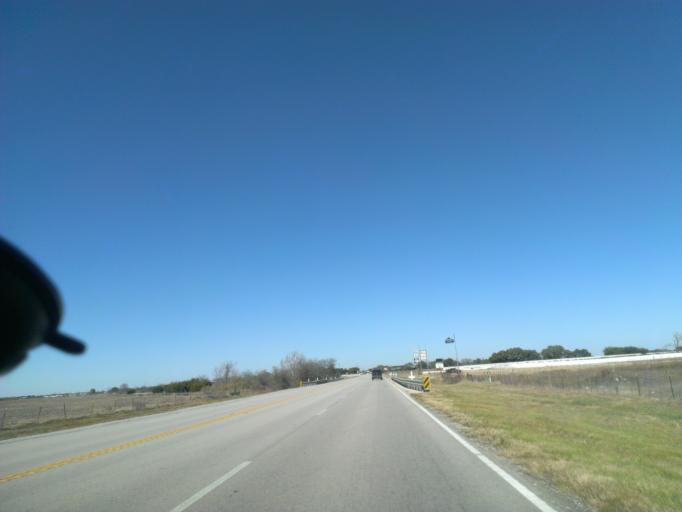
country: US
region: Texas
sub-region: Williamson County
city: Florence
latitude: 30.8785
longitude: -97.9190
